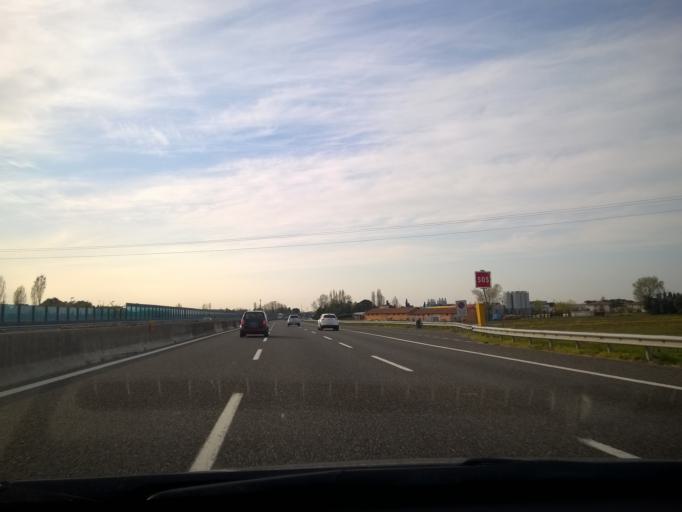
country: IT
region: Emilia-Romagna
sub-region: Forli-Cesena
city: San Mauro Pascoli
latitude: 44.1068
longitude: 12.4287
